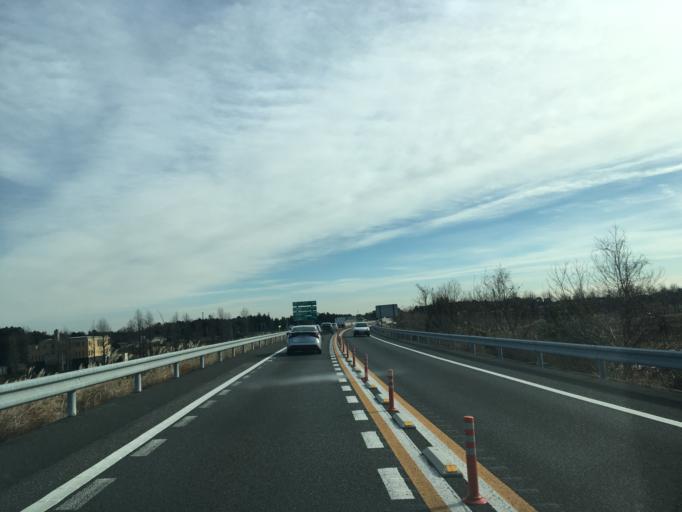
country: JP
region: Ibaraki
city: Naka
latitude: 36.0546
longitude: 140.0993
